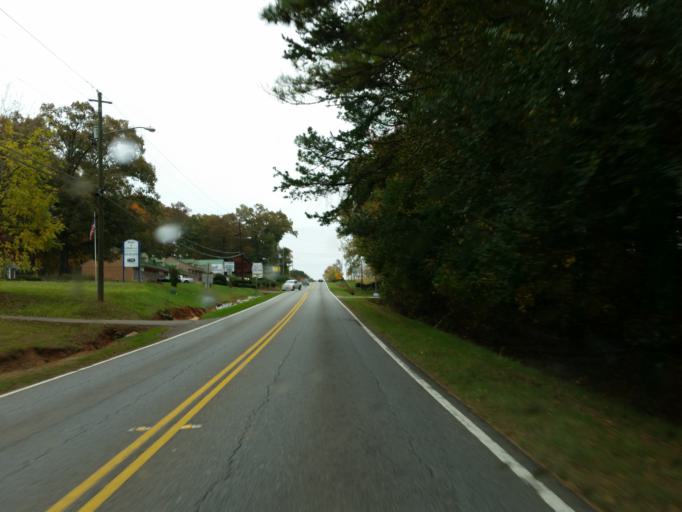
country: US
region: Georgia
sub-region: Pickens County
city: Jasper
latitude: 34.4658
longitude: -84.4434
